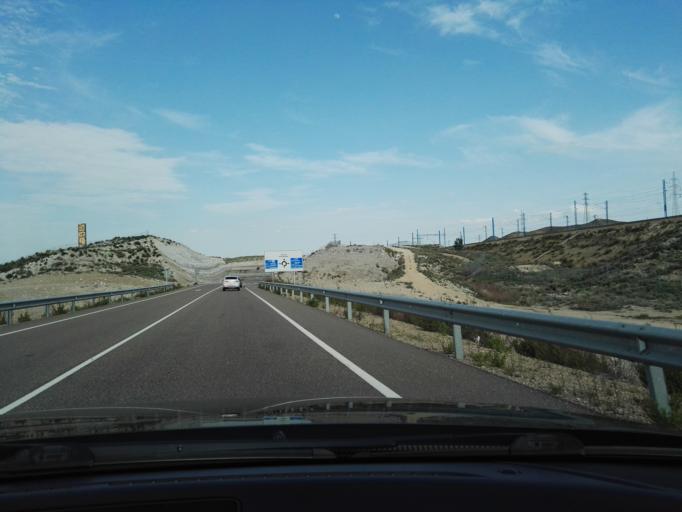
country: ES
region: Aragon
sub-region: Provincia de Zaragoza
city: Montecanal
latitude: 41.6182
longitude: -0.9644
